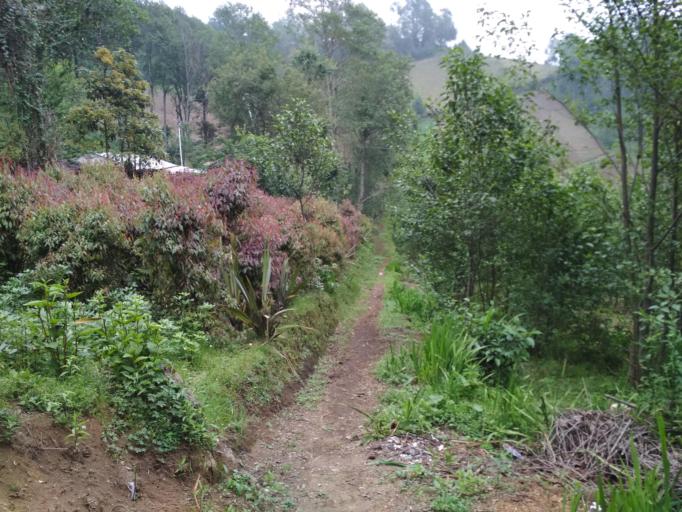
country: MX
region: Veracruz
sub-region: La Perla
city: Chilapa
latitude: 19.0005
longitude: -97.1664
